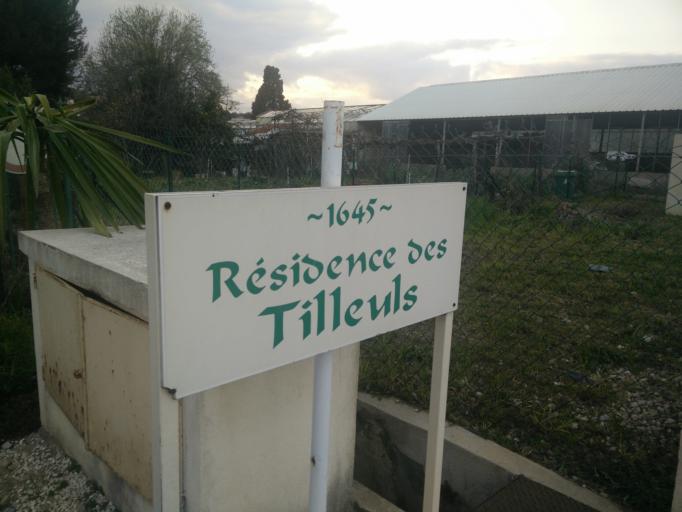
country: FR
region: Provence-Alpes-Cote d'Azur
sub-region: Departement des Alpes-Maritimes
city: Biot
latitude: 43.6015
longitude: 7.1126
